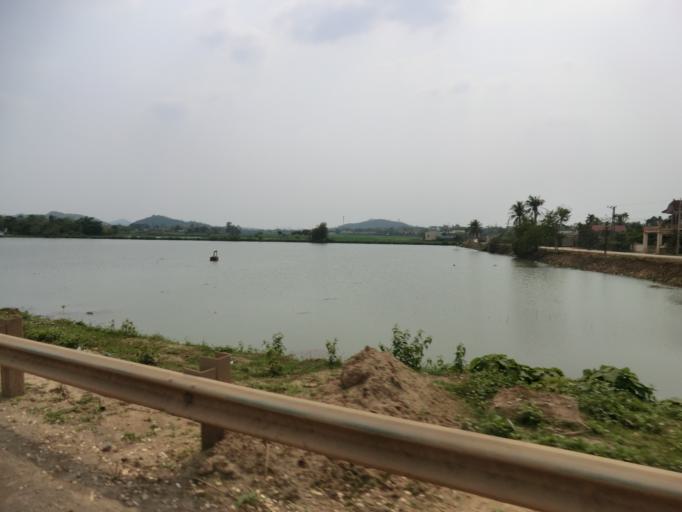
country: VN
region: Thanh Hoa
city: Thi Tran Yen Cat
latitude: 19.4184
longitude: 105.4503
